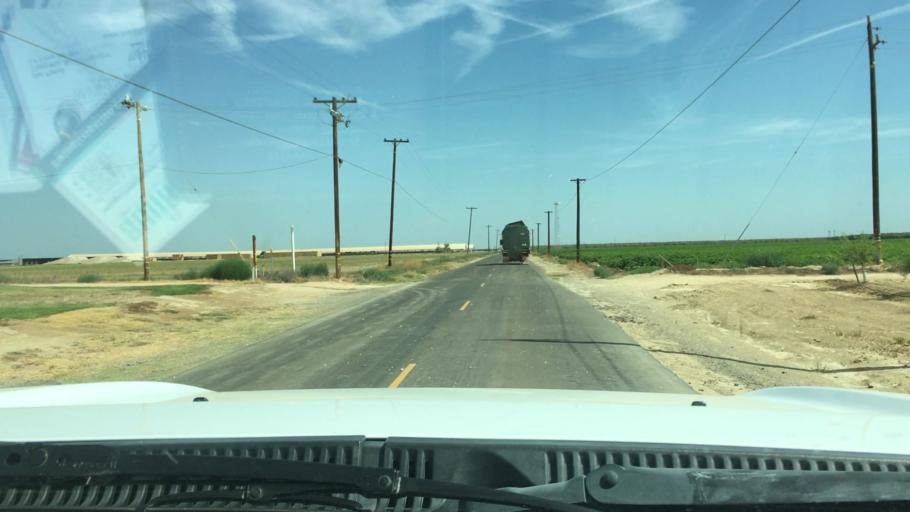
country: US
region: California
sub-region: Kern County
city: Shafter
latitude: 35.4635
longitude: -119.3681
